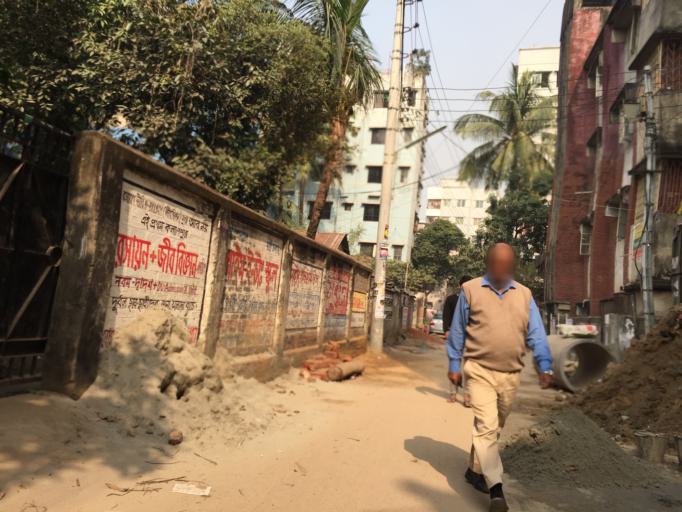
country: BD
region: Dhaka
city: Azimpur
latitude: 23.7874
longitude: 90.3611
